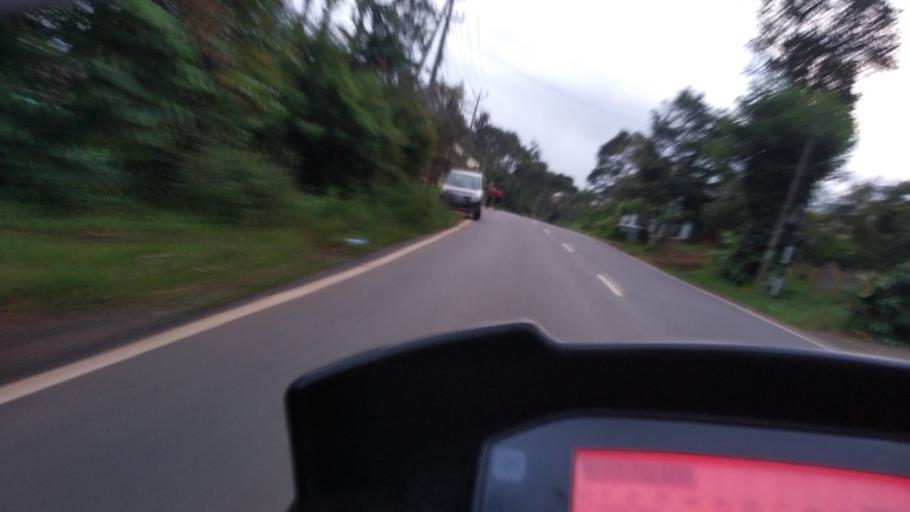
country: IN
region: Kerala
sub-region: Idukki
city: Munnar
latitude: 9.9692
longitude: 77.1292
